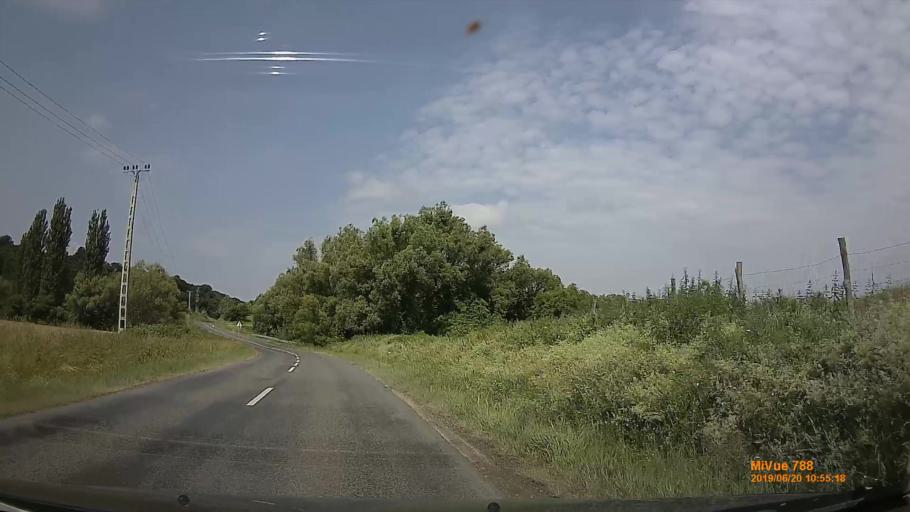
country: HU
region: Baranya
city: Mecseknadasd
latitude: 46.1545
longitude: 18.5527
